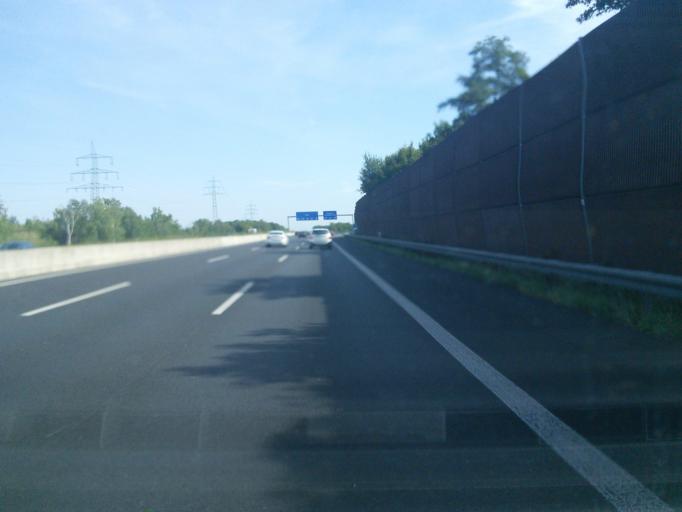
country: DE
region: North Rhine-Westphalia
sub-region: Regierungsbezirk Dusseldorf
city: Dusseldorf
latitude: 51.1599
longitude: 6.7465
